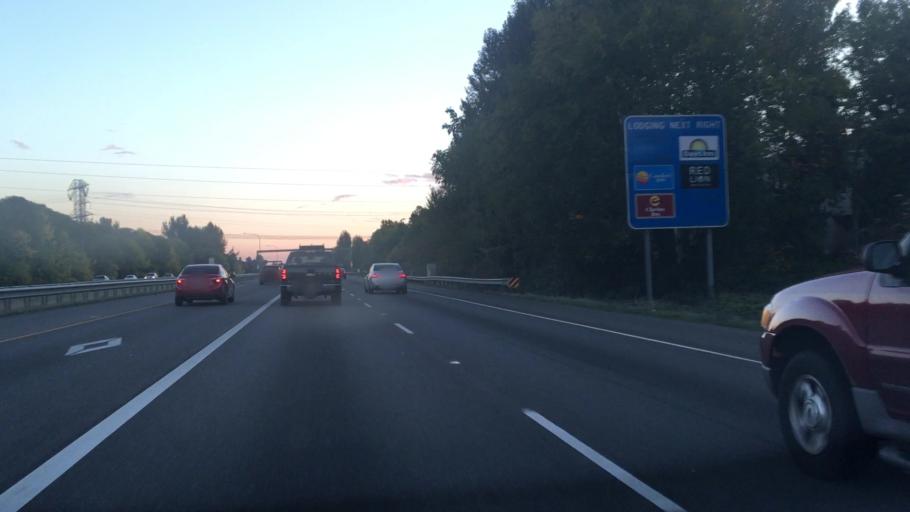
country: US
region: Washington
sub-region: King County
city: Lakeland North
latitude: 47.3388
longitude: -122.2451
